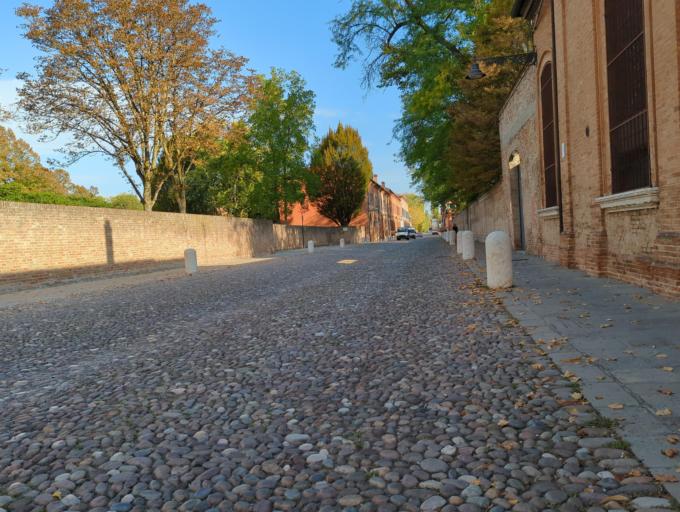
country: IT
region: Emilia-Romagna
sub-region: Provincia di Ferrara
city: Ferrara
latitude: 44.8430
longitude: 11.6218
